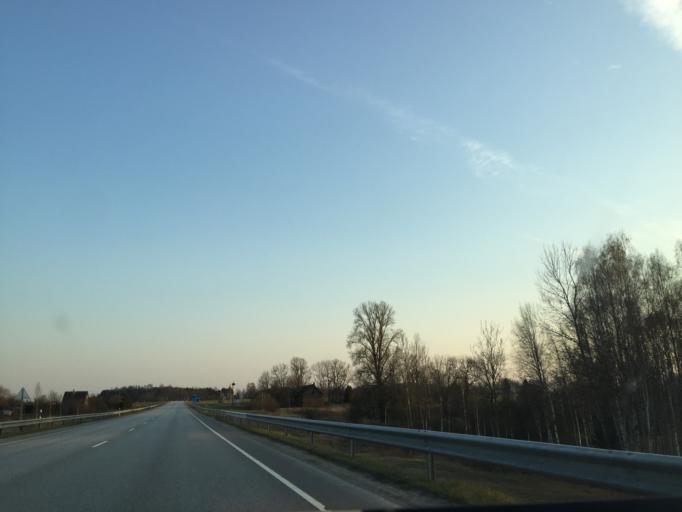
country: EE
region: Tartu
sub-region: Elva linn
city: Elva
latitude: 58.1939
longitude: 26.3518
